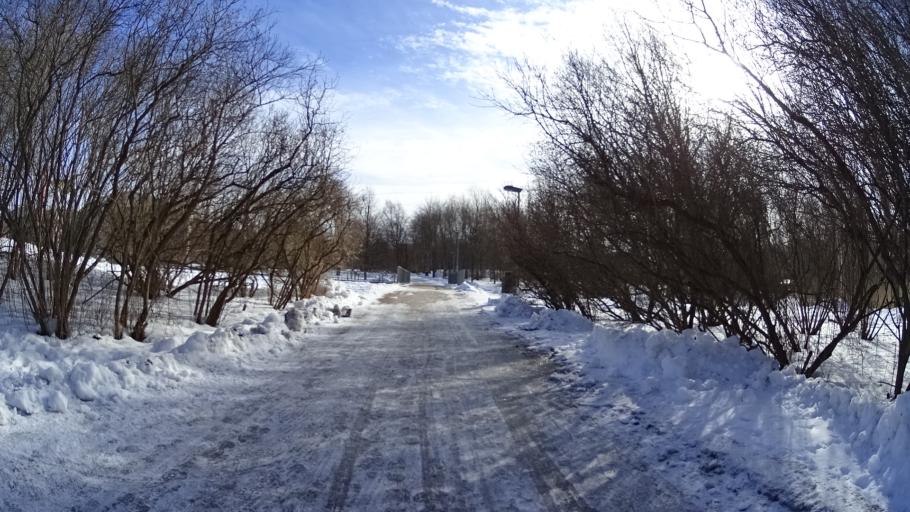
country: FI
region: Uusimaa
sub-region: Helsinki
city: Teekkarikylae
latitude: 60.2061
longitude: 24.8546
